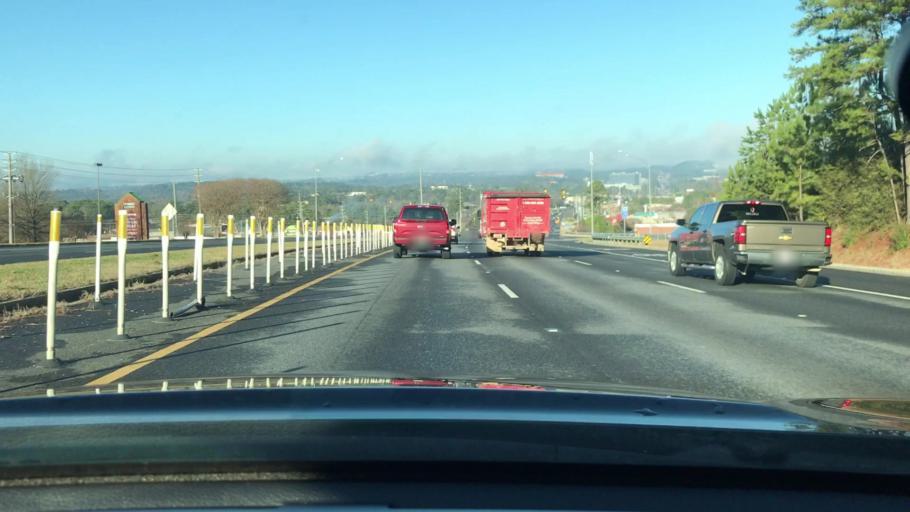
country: US
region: Alabama
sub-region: Shelby County
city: Lake Purdy
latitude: 33.4187
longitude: -86.6910
